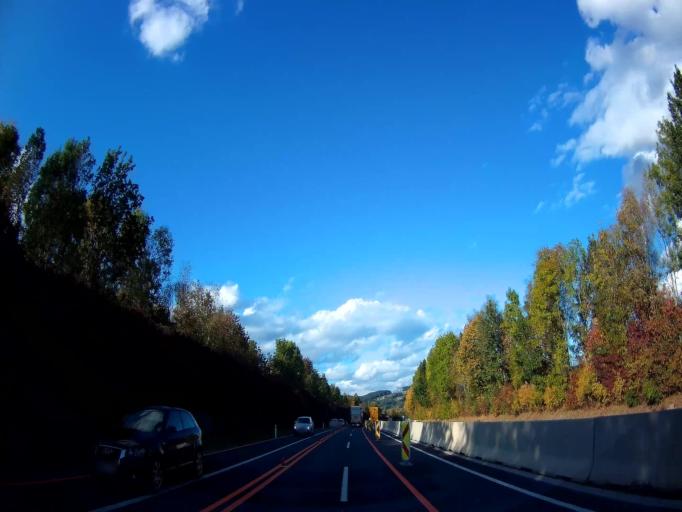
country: AT
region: Carinthia
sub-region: Politischer Bezirk Wolfsberg
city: Wolfsberg
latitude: 46.8291
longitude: 14.8181
